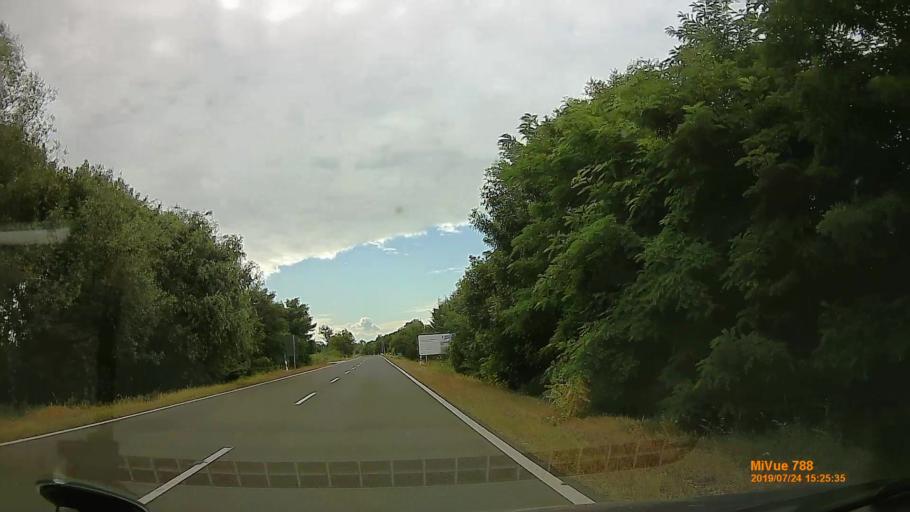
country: HU
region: Szabolcs-Szatmar-Bereg
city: Tarpa
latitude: 48.1595
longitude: 22.5392
